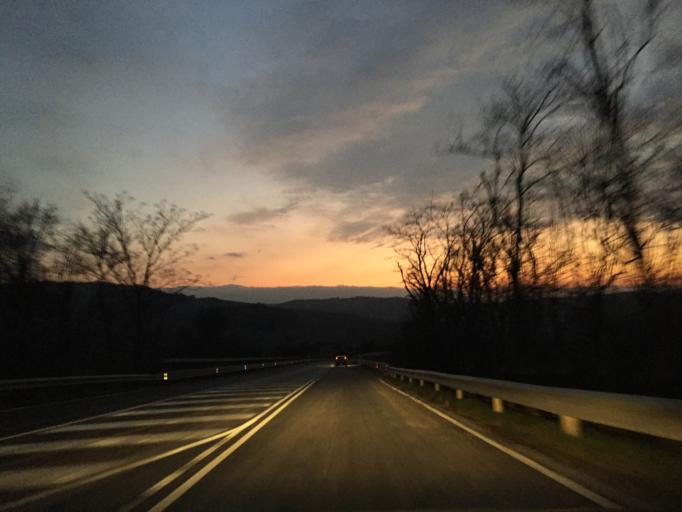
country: IT
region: Apulia
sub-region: Provincia di Foggia
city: Volturino
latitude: 41.4574
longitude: 15.0878
